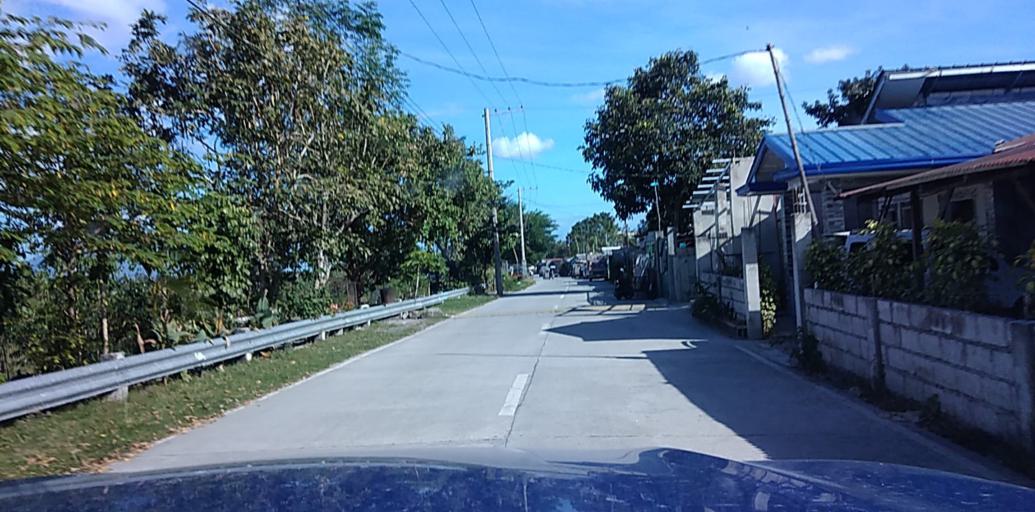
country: PH
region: Central Luzon
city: Santol
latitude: 15.1505
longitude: 120.5422
